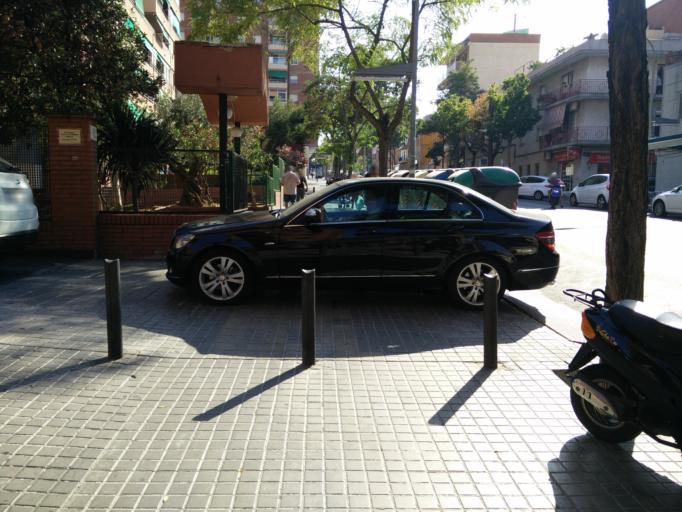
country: ES
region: Catalonia
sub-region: Provincia de Barcelona
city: Llefia
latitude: 41.4511
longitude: 2.2268
